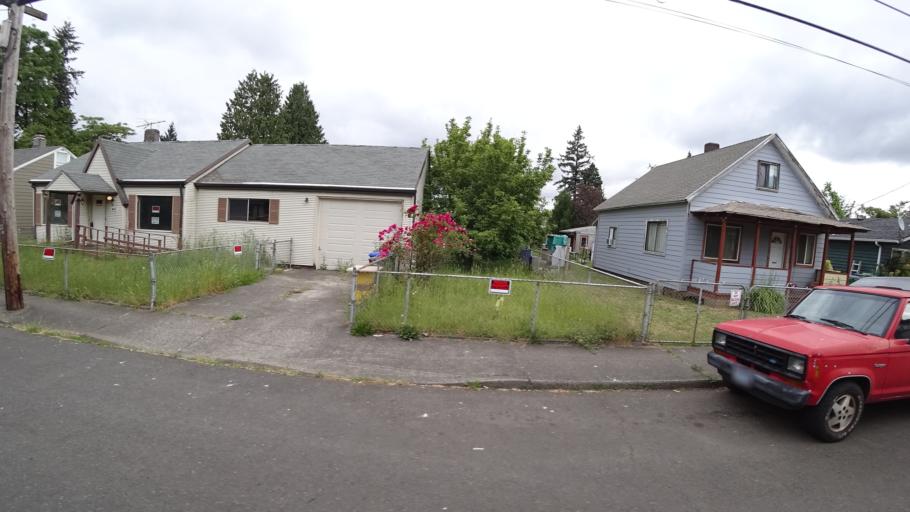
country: US
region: Oregon
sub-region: Multnomah County
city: Lents
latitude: 45.4782
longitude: -122.5807
